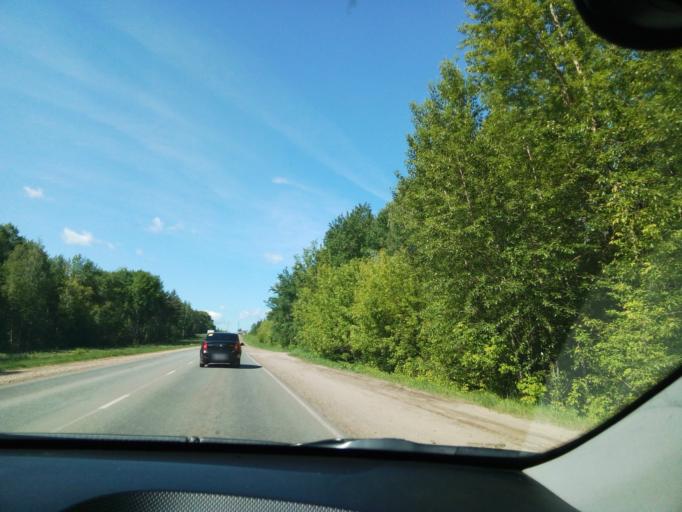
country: RU
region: Chuvashia
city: Novocheboksarsk
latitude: 56.0801
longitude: 47.5023
